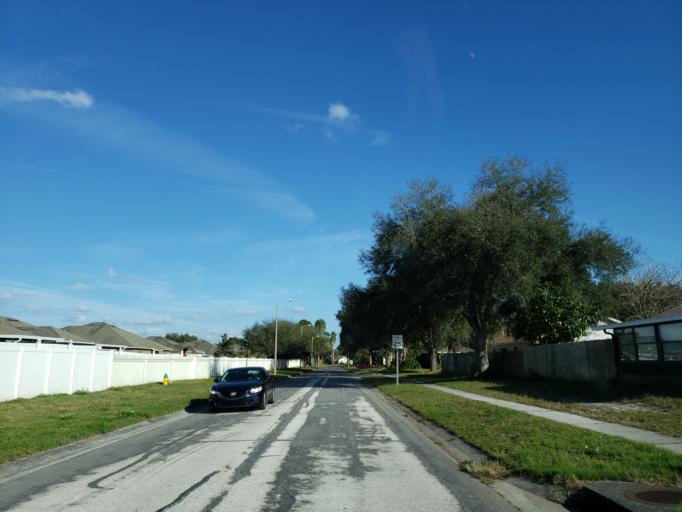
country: US
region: Florida
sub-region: Hillsborough County
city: Balm
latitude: 27.7903
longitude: -82.3233
